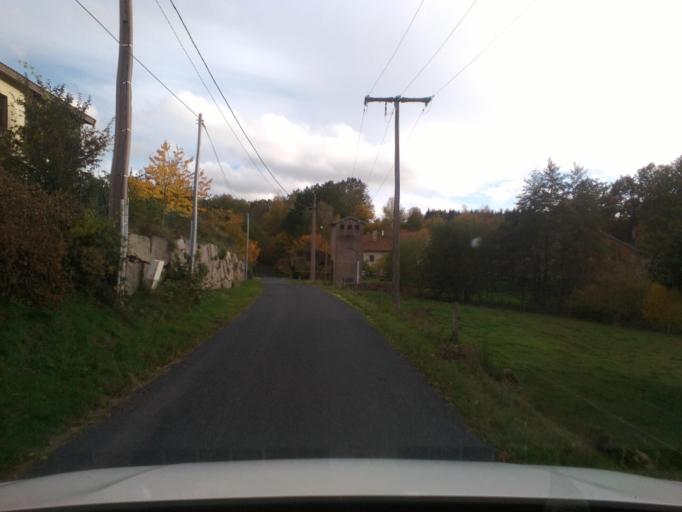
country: FR
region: Lorraine
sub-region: Departement des Vosges
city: Senones
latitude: 48.3536
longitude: 7.0203
